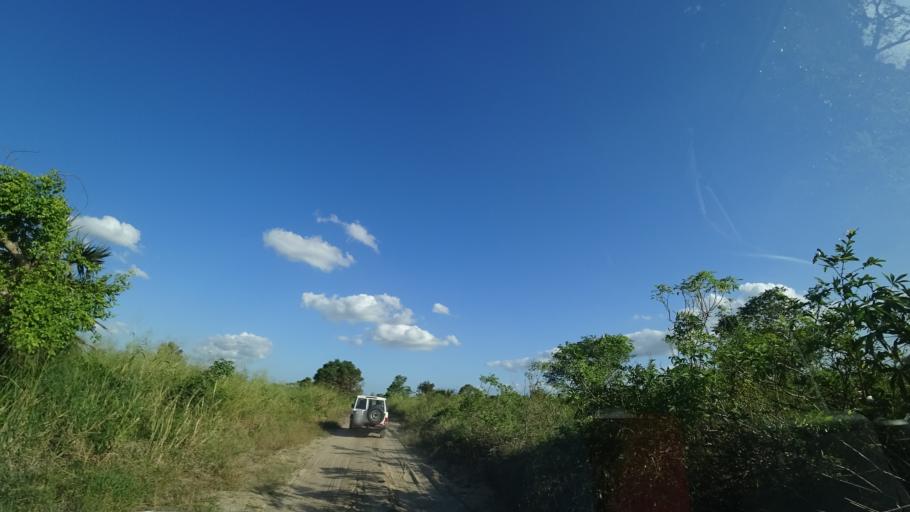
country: MZ
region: Sofala
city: Dondo
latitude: -19.3823
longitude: 34.5924
